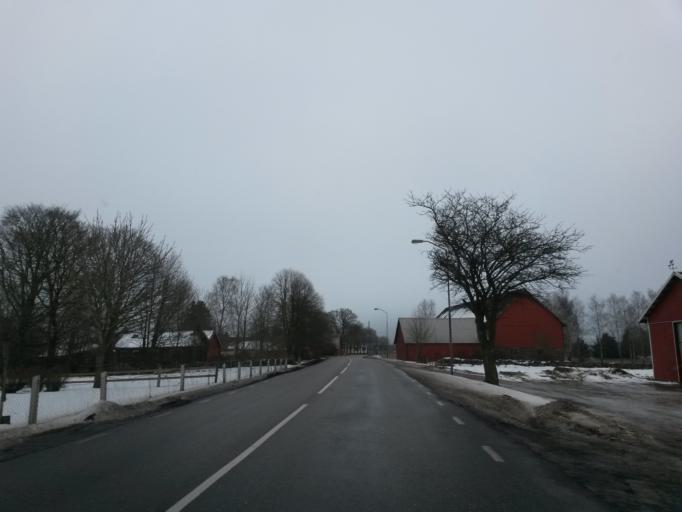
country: SE
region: Vaestra Goetaland
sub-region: Herrljunga Kommun
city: Herrljunga
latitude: 57.9898
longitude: 13.0184
